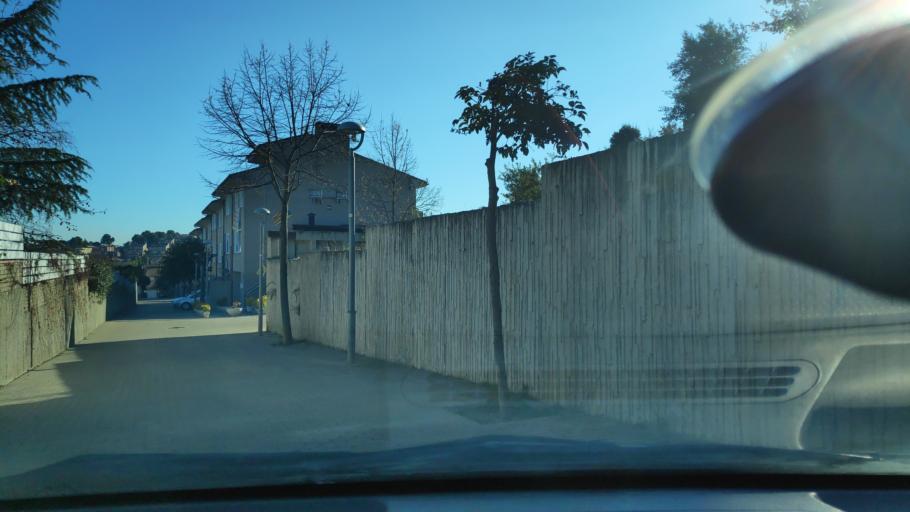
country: ES
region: Catalonia
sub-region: Provincia de Barcelona
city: Sant Quirze del Valles
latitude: 41.5295
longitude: 2.0684
